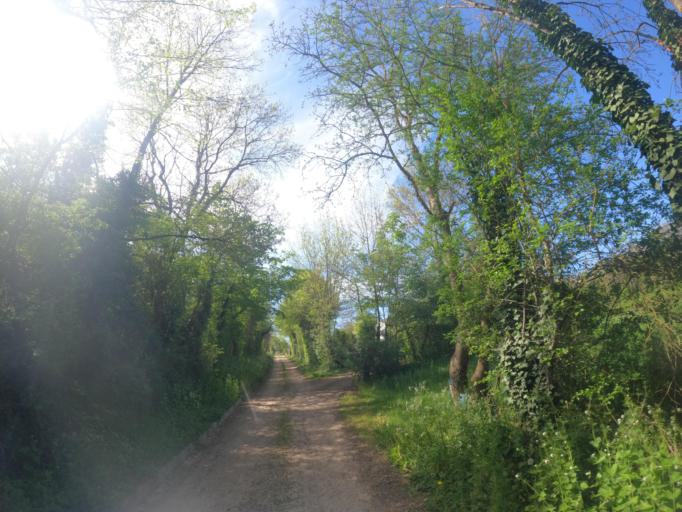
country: FR
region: Poitou-Charentes
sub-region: Departement des Deux-Sevres
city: Saint-Varent
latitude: 46.9135
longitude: -0.2095
